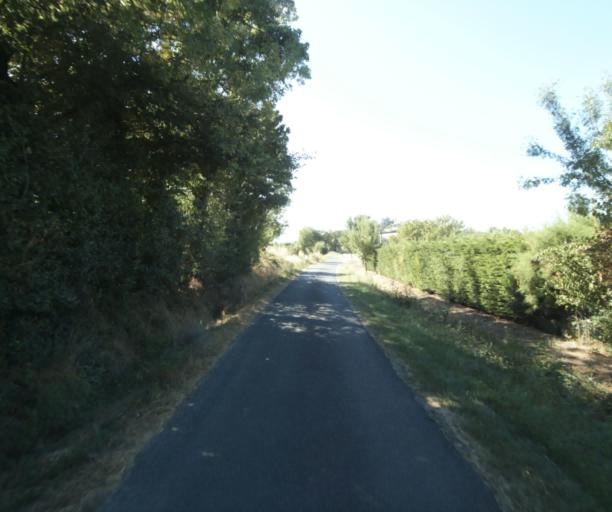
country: FR
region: Midi-Pyrenees
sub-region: Departement de la Haute-Garonne
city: Saint-Felix-Lauragais
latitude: 43.5053
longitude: 1.9410
